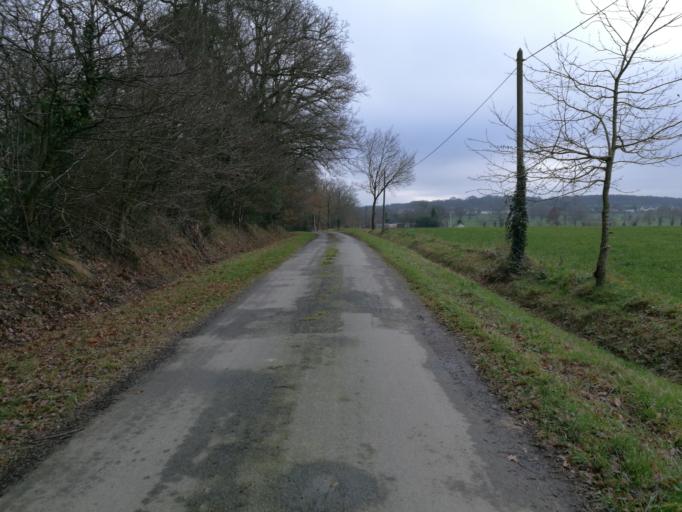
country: FR
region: Brittany
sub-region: Departement d'Ille-et-Vilaine
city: Le Theil-de-Bretagne
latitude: 47.9251
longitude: -1.4070
